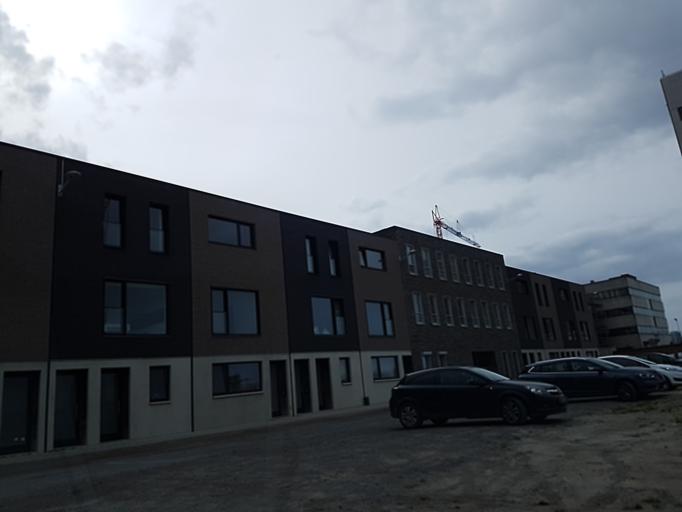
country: BE
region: Flanders
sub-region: Provincie West-Vlaanderen
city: Ostend
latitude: 51.2236
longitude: 2.9497
